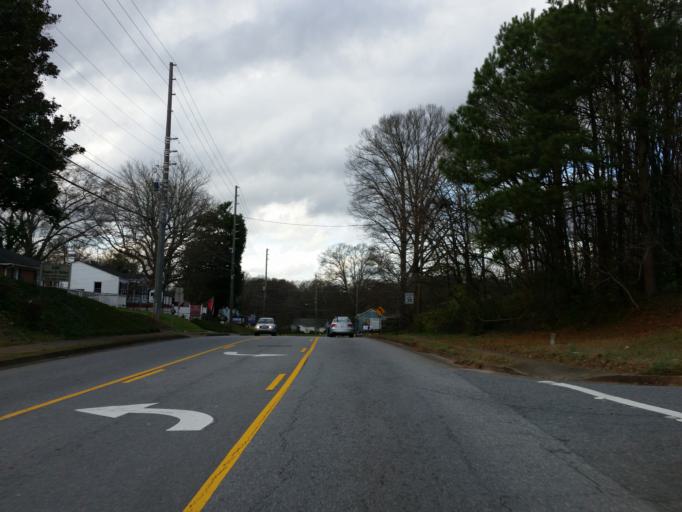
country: US
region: Georgia
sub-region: Cobb County
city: Marietta
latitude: 33.9472
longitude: -84.5001
